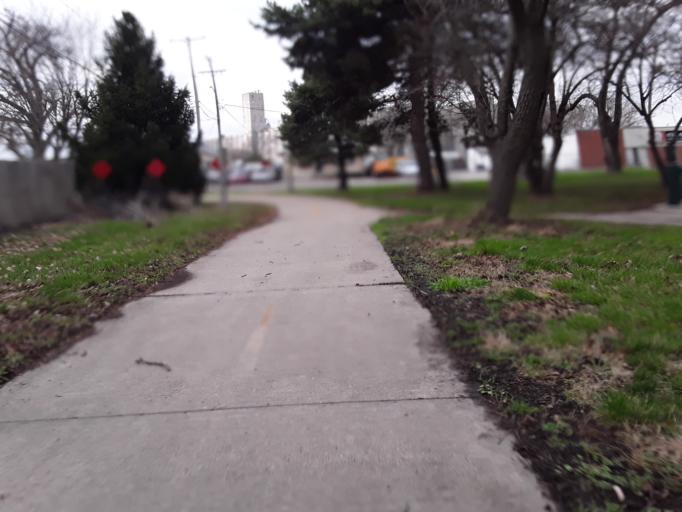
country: US
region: Nebraska
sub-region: Lancaster County
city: Lincoln
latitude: 40.8399
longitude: -96.6722
